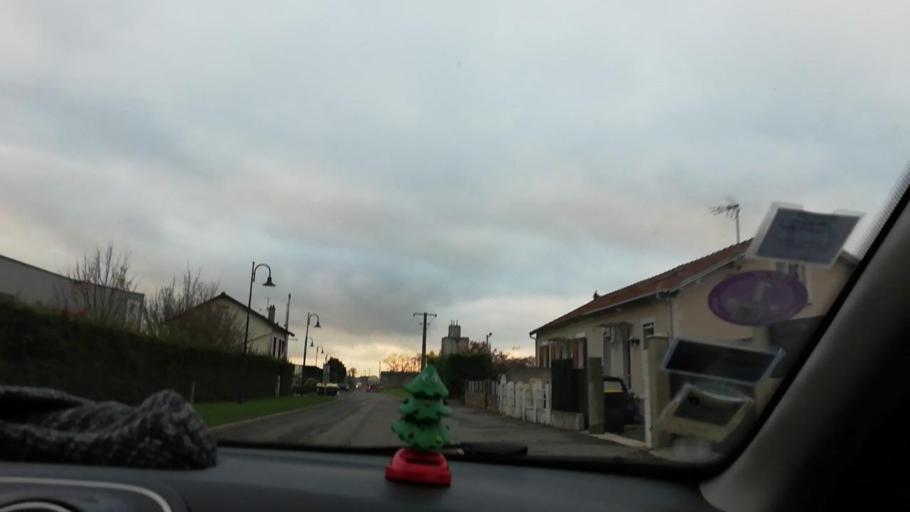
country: FR
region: Ile-de-France
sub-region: Departement de Seine-et-Marne
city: Charny
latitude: 48.9685
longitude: 2.7550
